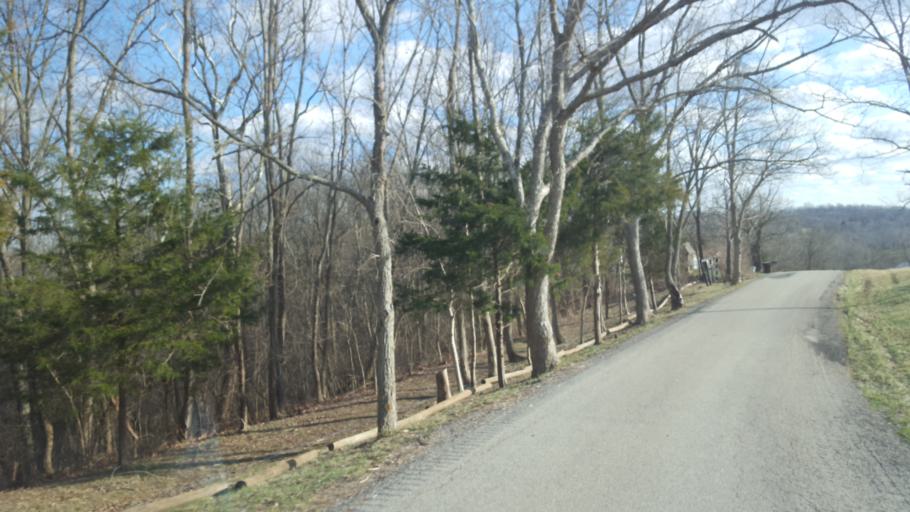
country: US
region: Kentucky
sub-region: Scott County
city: Georgetown
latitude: 38.3253
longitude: -84.5098
